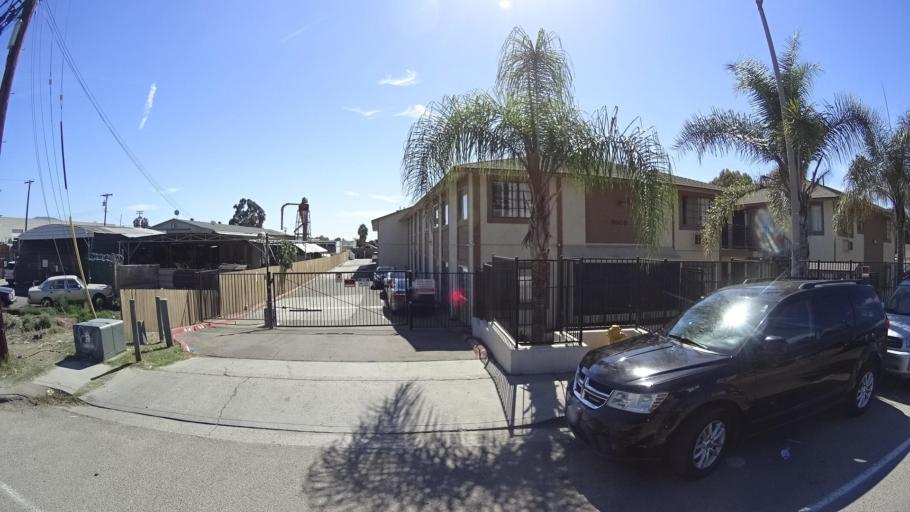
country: US
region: California
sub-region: San Diego County
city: La Presa
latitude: 32.7185
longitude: -117.0045
